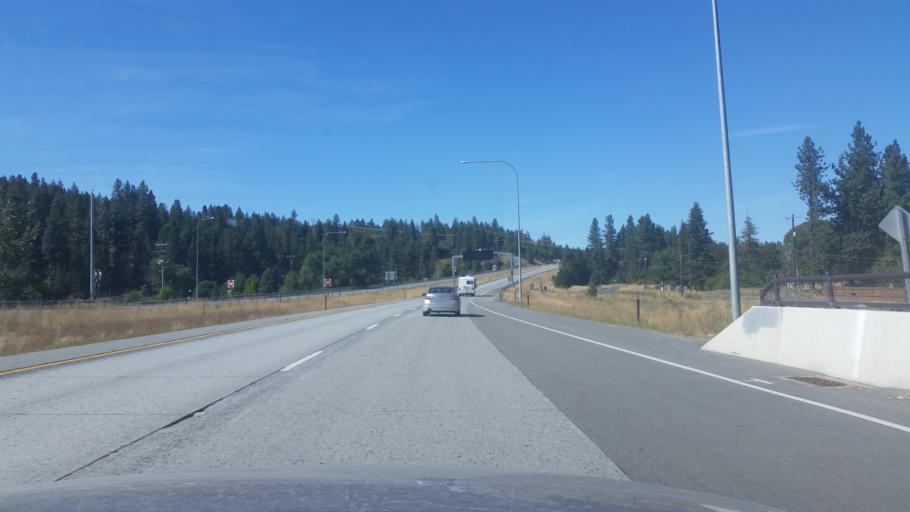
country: US
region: Washington
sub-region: Spokane County
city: Spokane
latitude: 47.6233
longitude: -117.4381
